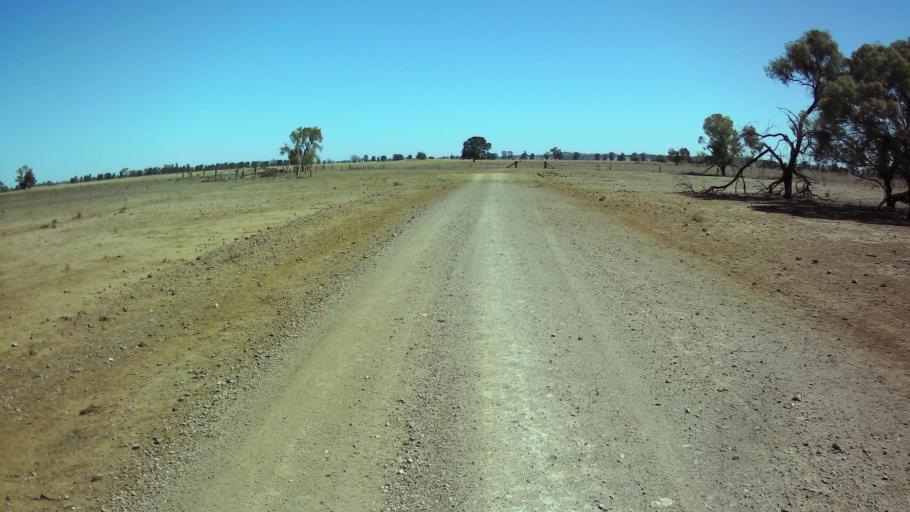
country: AU
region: New South Wales
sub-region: Forbes
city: Forbes
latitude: -33.7259
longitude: 147.6657
